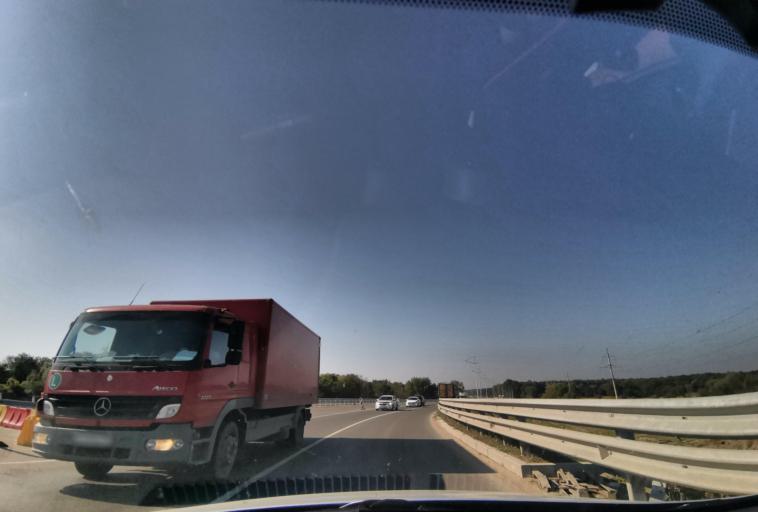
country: RU
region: Kaliningrad
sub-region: Gorod Kaliningrad
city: Kaliningrad
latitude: 54.7672
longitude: 20.4897
